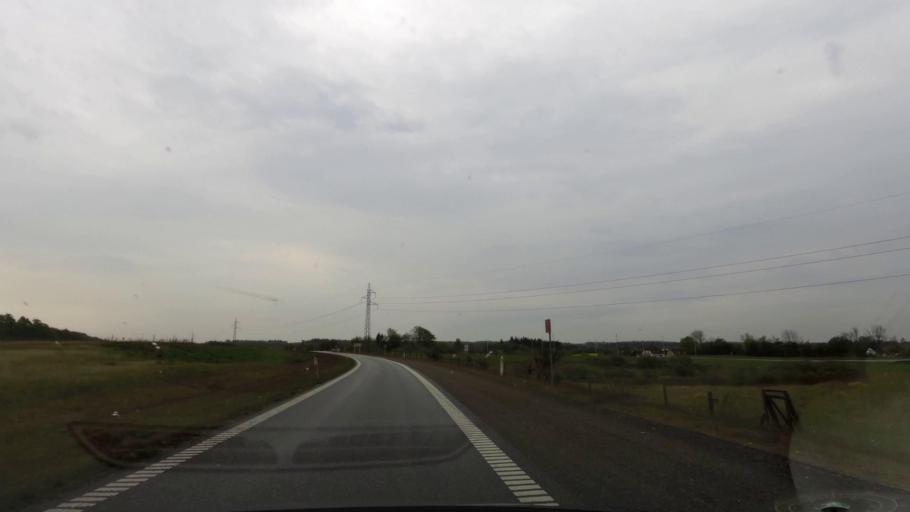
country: DK
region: South Denmark
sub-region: Svendborg Kommune
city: Svendborg
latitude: 55.1151
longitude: 10.5600
